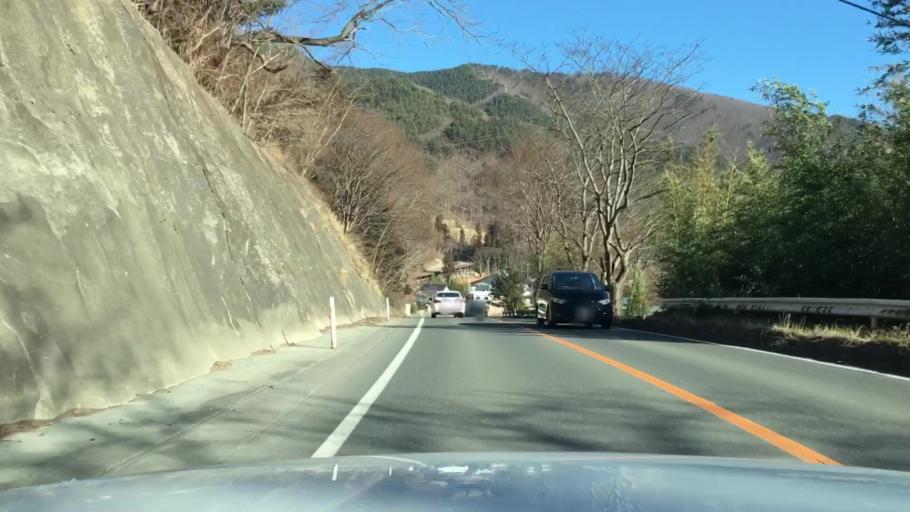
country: JP
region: Iwate
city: Miyako
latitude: 39.5958
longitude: 141.6767
